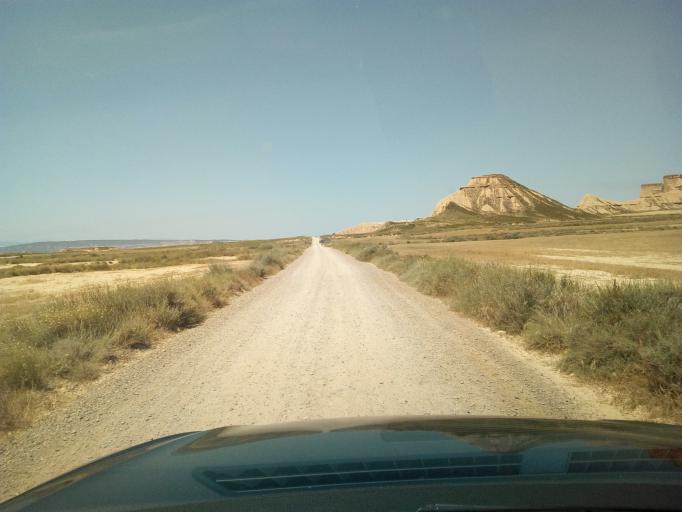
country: ES
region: Aragon
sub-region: Provincia de Zaragoza
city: Sadaba
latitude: 42.1943
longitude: -1.4141
